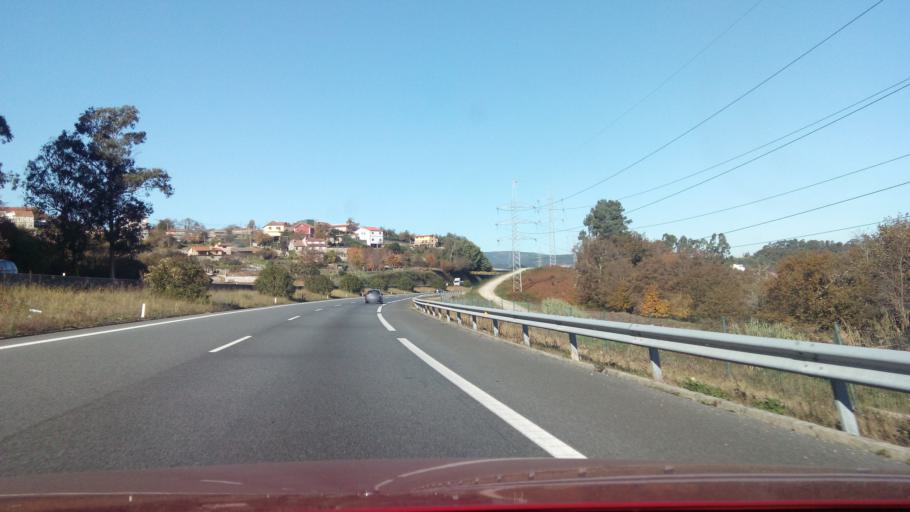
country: ES
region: Galicia
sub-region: Provincia de Pontevedra
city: Pontevedra
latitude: 42.3972
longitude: -8.6476
